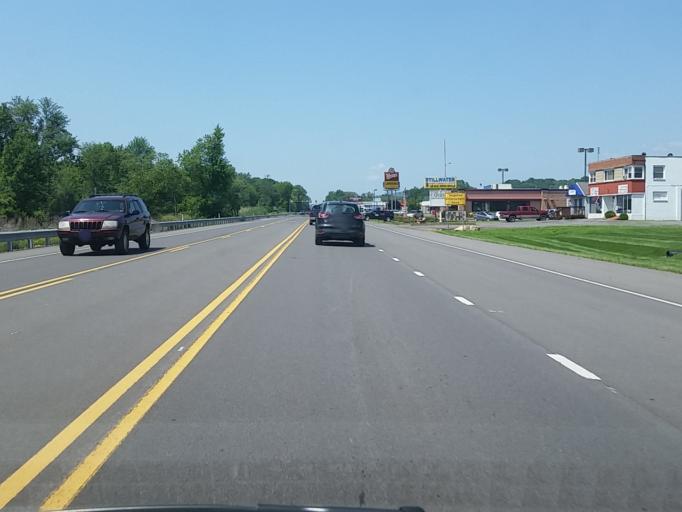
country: US
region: Pennsylvania
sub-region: Columbia County
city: Espy
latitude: 41.0096
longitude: -76.4195
